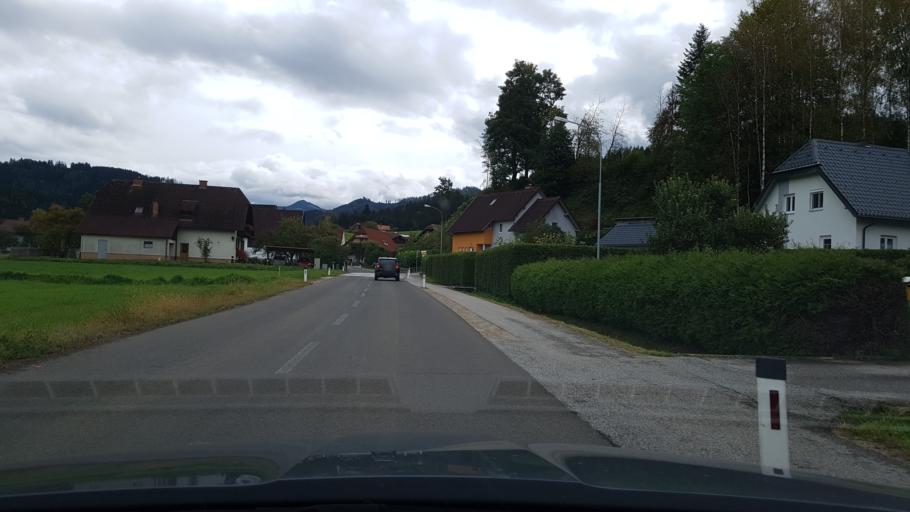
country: AT
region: Styria
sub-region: Politischer Bezirk Bruck-Muerzzuschlag
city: Allerheiligen im Muerztal
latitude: 47.4764
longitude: 15.4098
